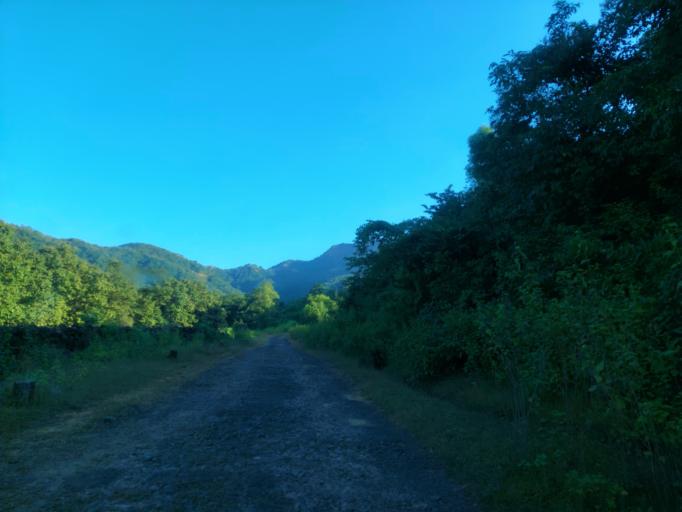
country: IN
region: Maharashtra
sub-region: Sindhudurg
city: Kudal
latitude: 16.0753
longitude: 73.8260
